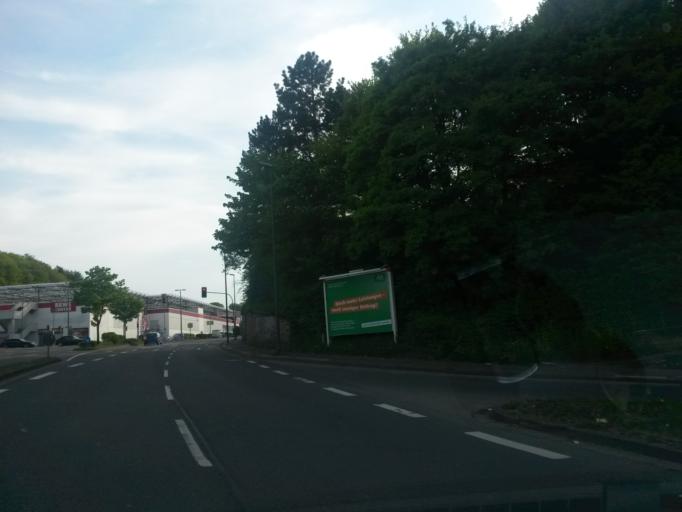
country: DE
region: North Rhine-Westphalia
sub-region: Regierungsbezirk Arnsberg
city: Luedenscheid
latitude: 51.2274
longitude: 7.6348
